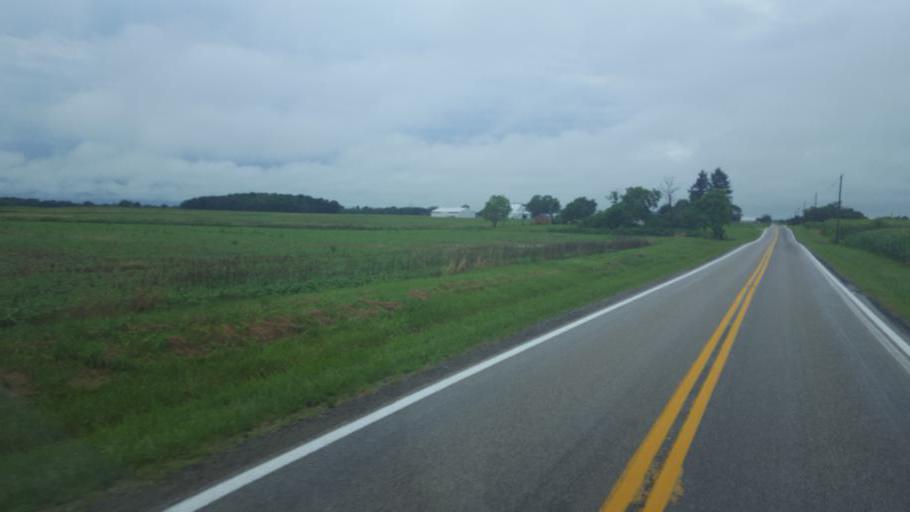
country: US
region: Ohio
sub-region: Union County
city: Richwood
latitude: 40.5200
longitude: -83.3454
